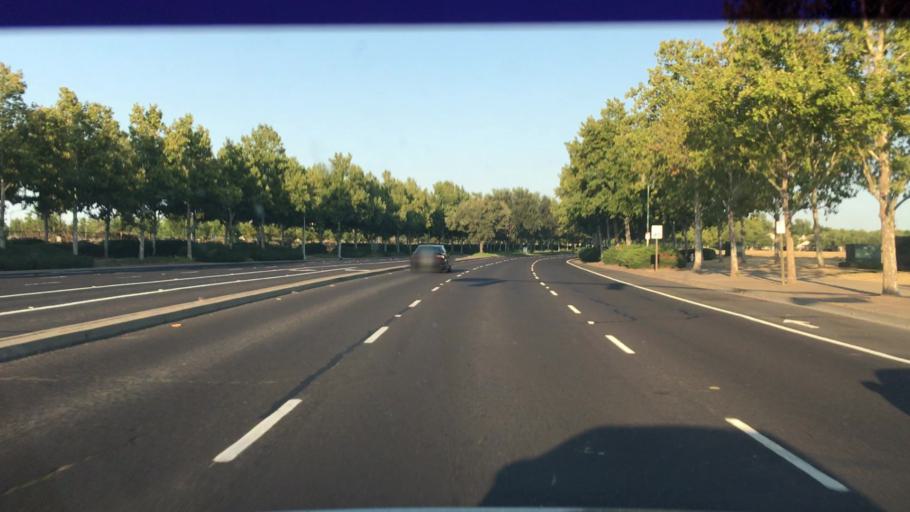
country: US
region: California
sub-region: Sacramento County
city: Laguna
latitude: 38.4279
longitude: -121.4698
